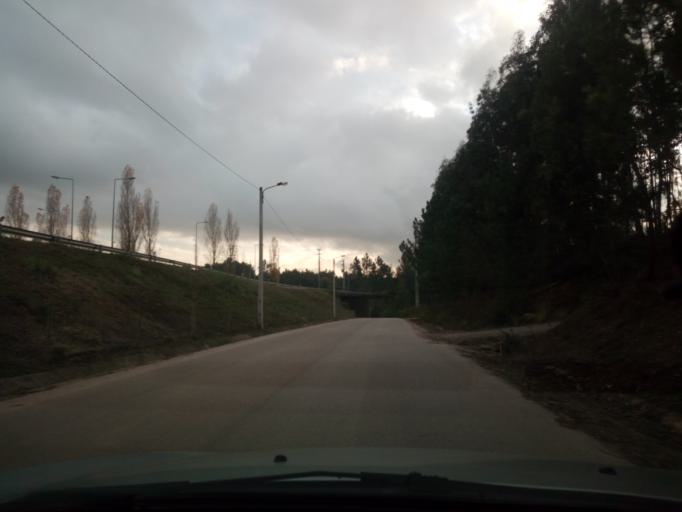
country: PT
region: Aveiro
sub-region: Agueda
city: Agueda
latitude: 40.5552
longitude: -8.4754
